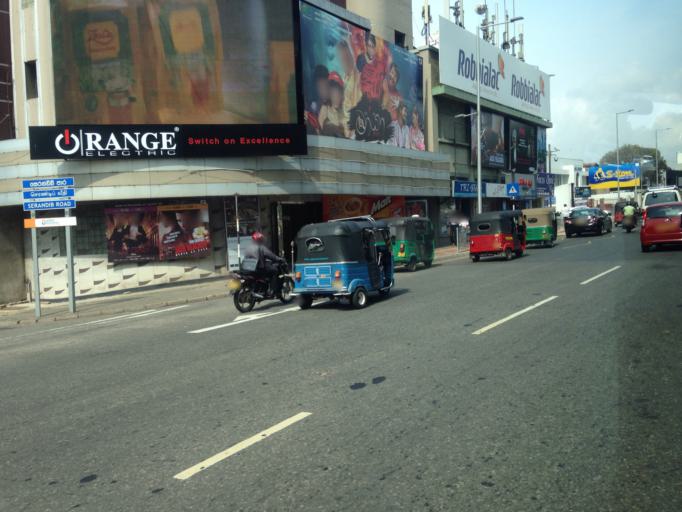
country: LK
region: Western
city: Colombo
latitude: 6.9121
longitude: 79.8509
